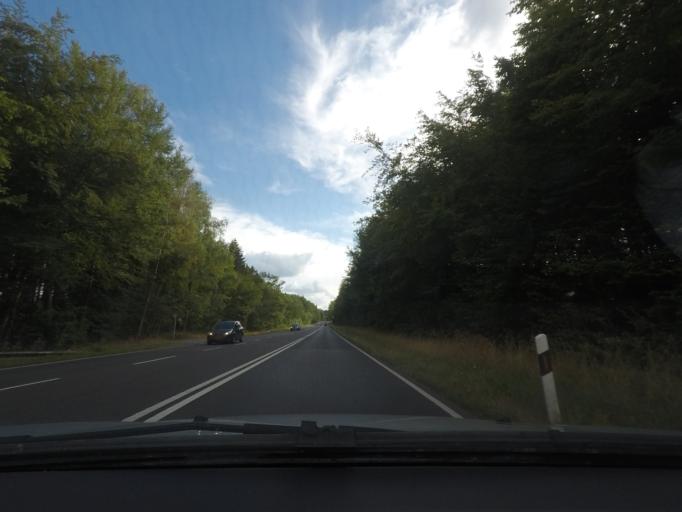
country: LU
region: Grevenmacher
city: Gonderange
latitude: 49.6793
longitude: 6.2201
